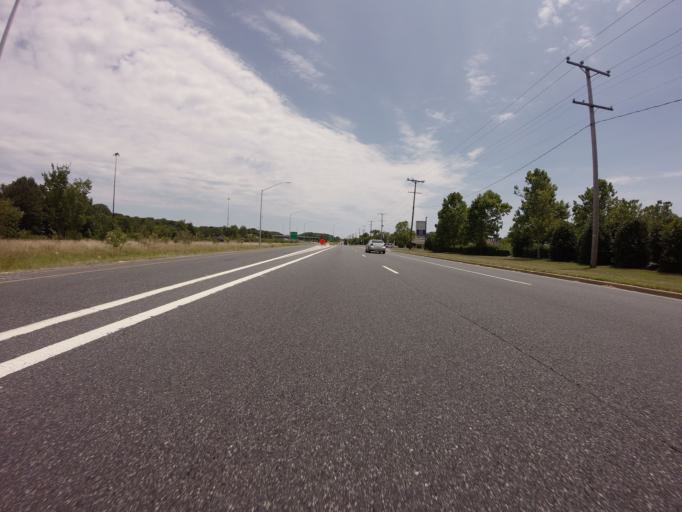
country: US
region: Maryland
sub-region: Baltimore County
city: Essex
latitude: 39.2857
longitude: -76.4959
